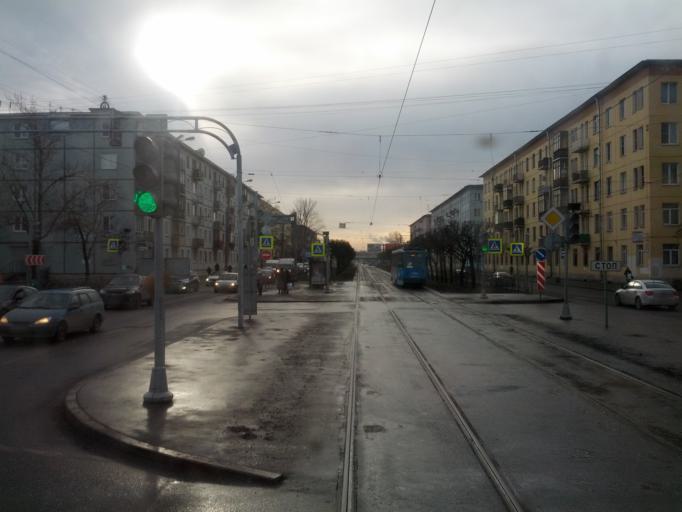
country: RU
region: St.-Petersburg
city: Centralniy
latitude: 59.9225
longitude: 30.4192
